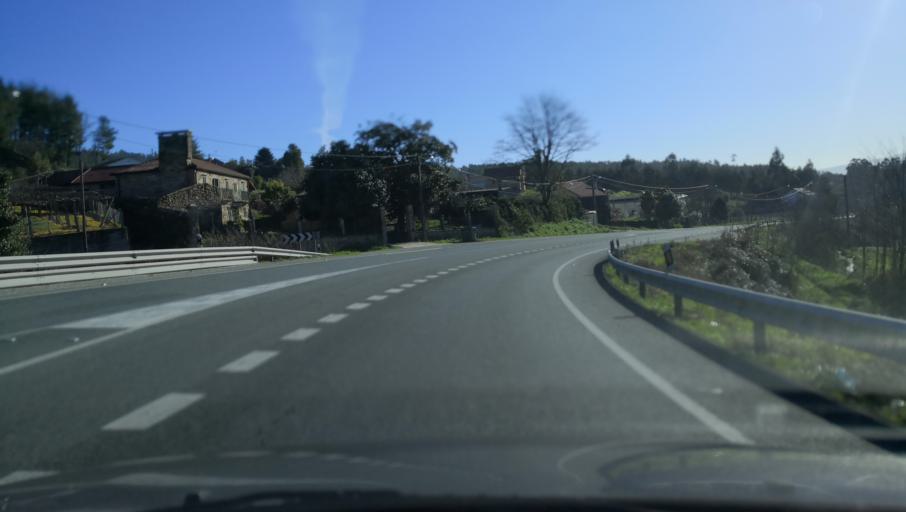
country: ES
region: Galicia
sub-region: Provincia da Coruna
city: Vedra
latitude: 42.7932
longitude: -8.4507
